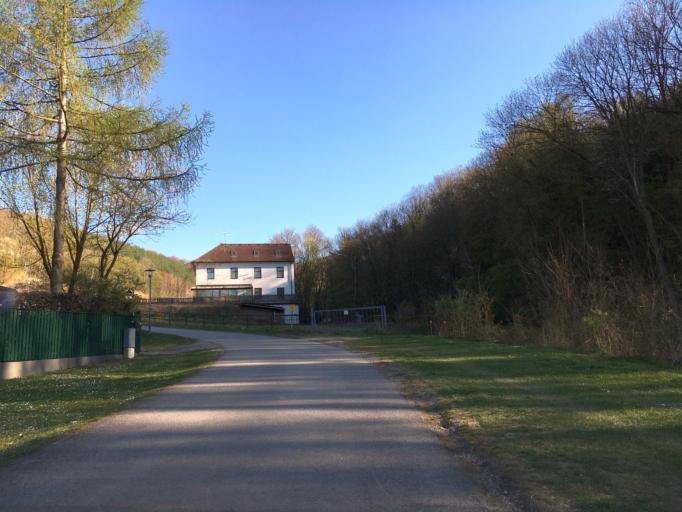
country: AT
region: Lower Austria
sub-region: Politischer Bezirk Tulln
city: Konigstetten
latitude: 48.2952
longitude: 16.1538
